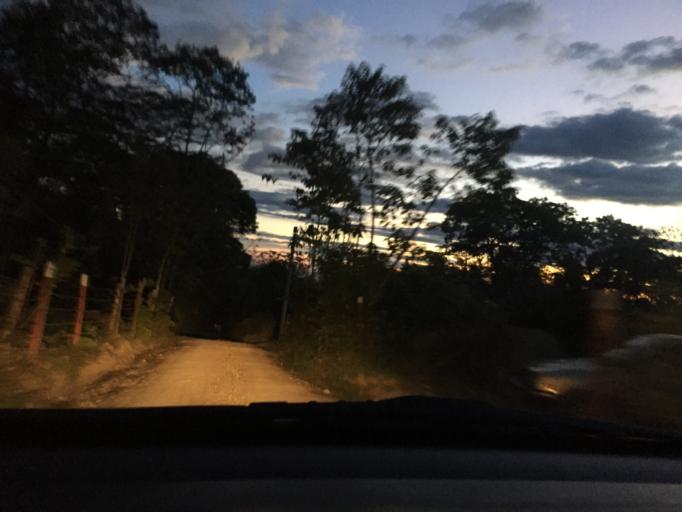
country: CO
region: Cundinamarca
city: Zipacon
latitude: 4.7237
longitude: -74.4212
